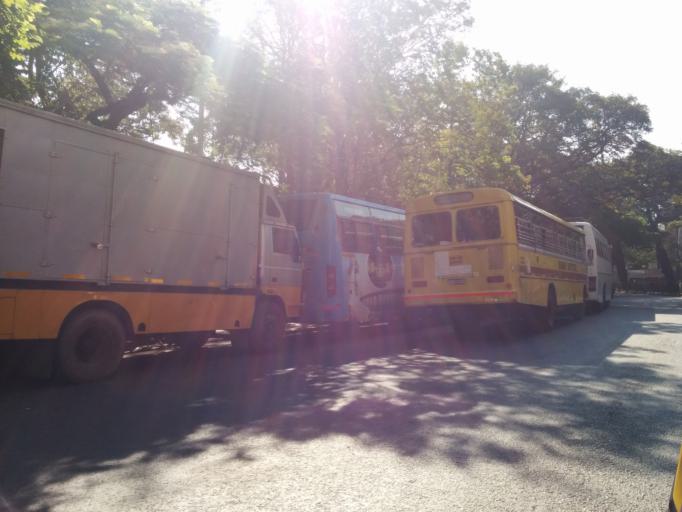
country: IN
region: Maharashtra
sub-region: Raigarh
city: Uran
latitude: 18.9271
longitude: 72.8314
